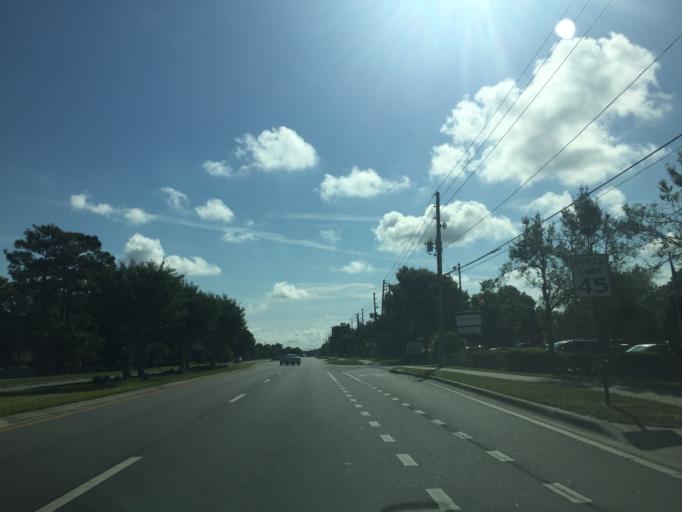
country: US
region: Florida
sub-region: Seminole County
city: Goldenrod
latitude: 28.6475
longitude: -81.2750
